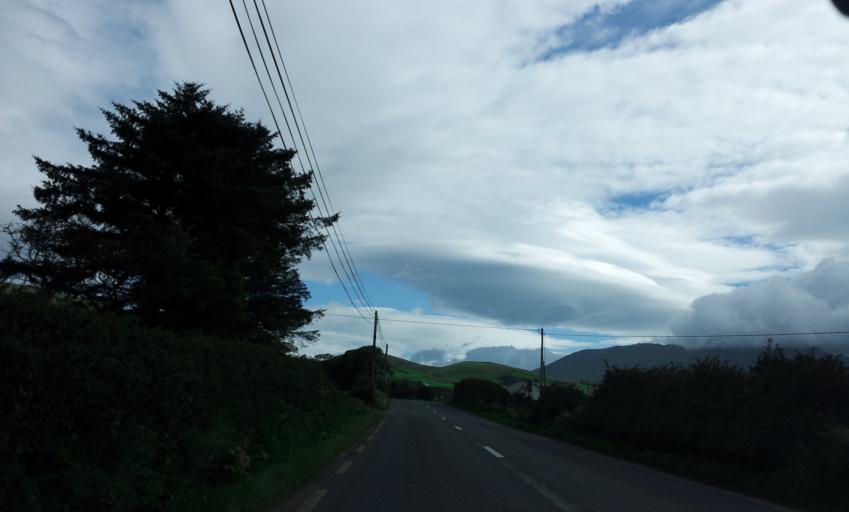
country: IE
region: Munster
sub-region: Ciarrai
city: Killorglin
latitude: 52.1855
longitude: -9.9567
